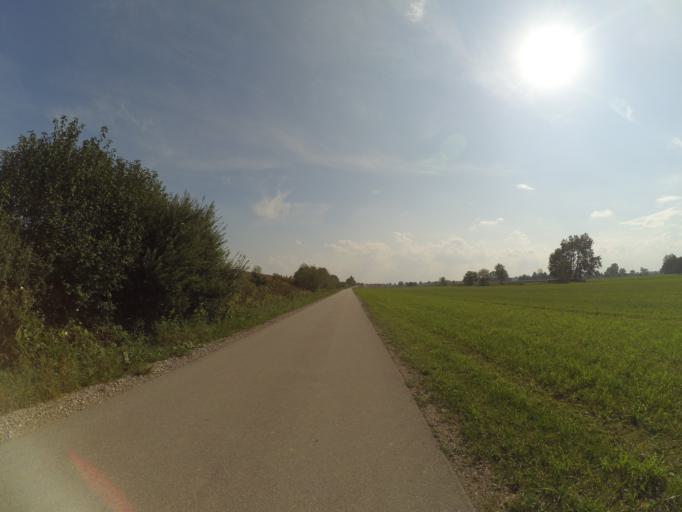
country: DE
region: Bavaria
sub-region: Swabia
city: Lamerdingen
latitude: 48.0720
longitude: 10.7289
